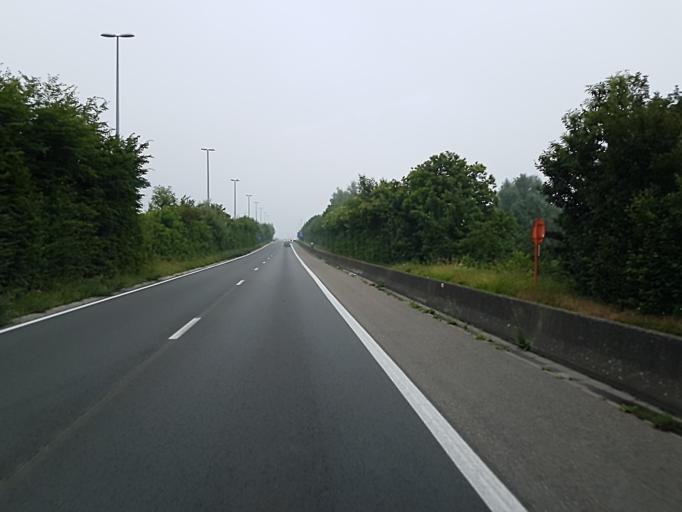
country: FR
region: Nord-Pas-de-Calais
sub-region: Departement du Nord
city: Halluin
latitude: 50.7915
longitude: 3.1384
